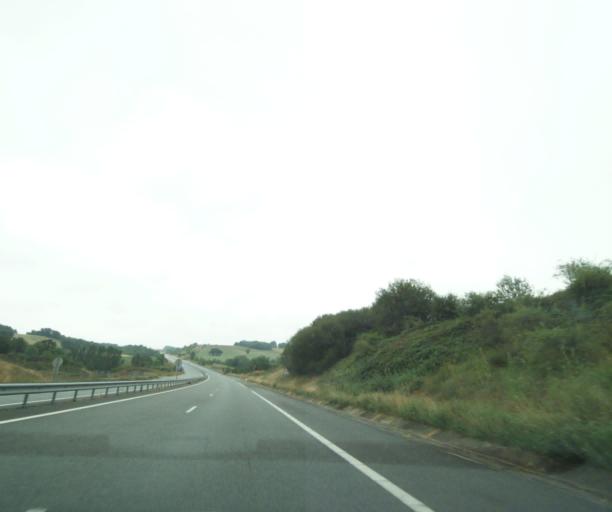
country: FR
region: Midi-Pyrenees
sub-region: Departement du Tarn
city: Carmaux
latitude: 44.0387
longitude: 2.2058
